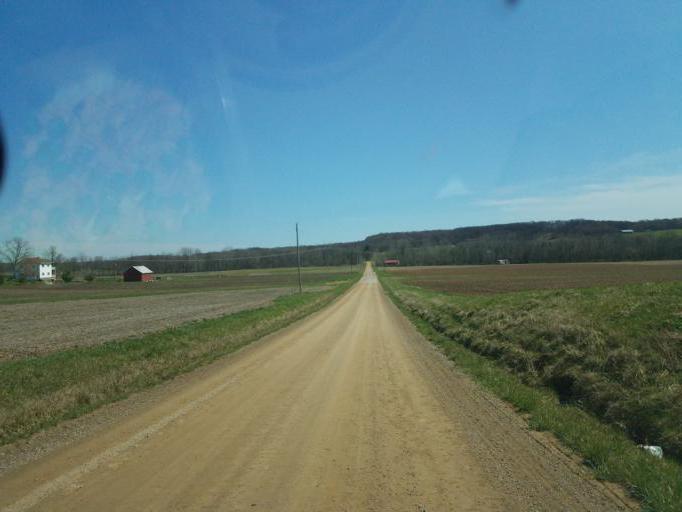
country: US
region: Ohio
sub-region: Knox County
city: Oak Hill
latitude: 40.3053
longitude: -82.2451
